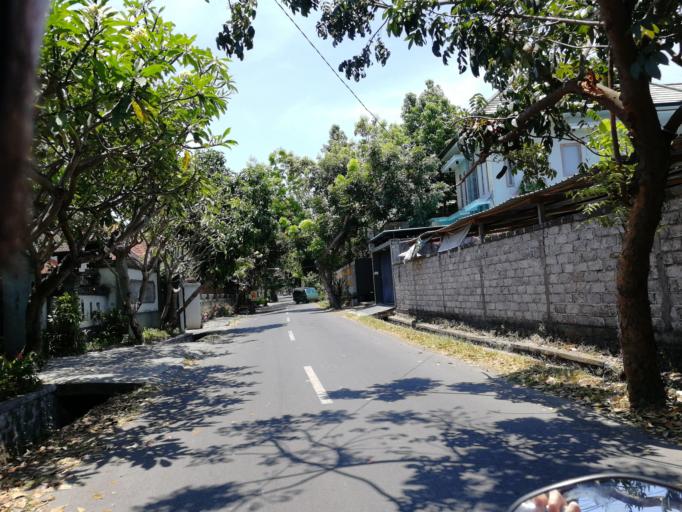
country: ID
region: Bali
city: Dajan Tangluk
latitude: -8.6658
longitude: 115.2367
